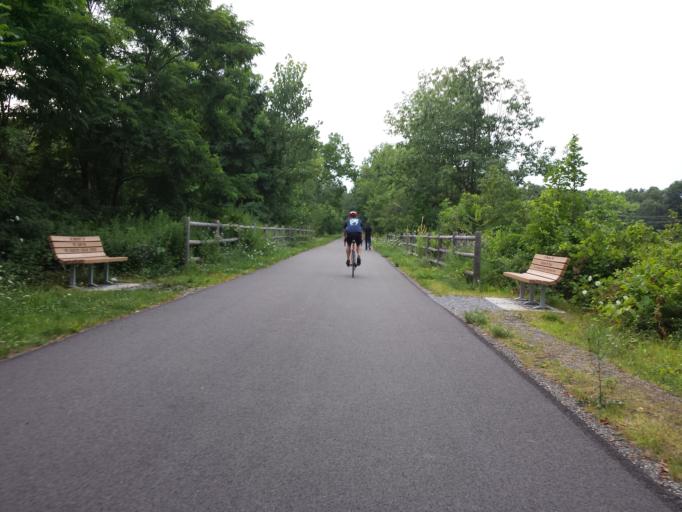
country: US
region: New York
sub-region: Dutchess County
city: Arlington
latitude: 41.6884
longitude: -73.8762
